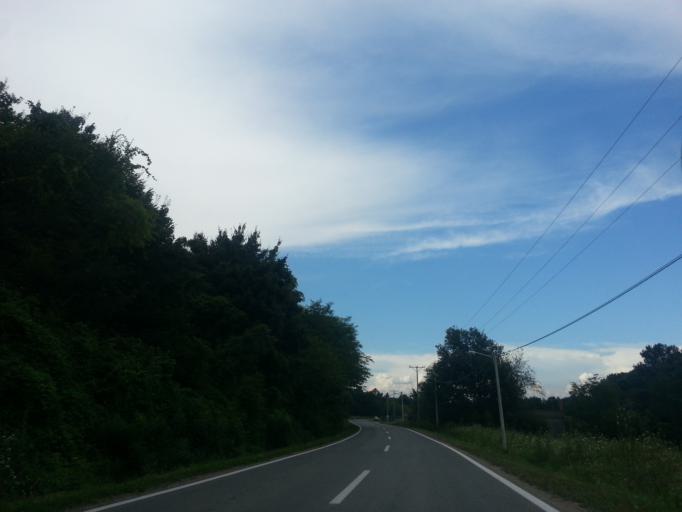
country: BA
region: Brcko
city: Brcko
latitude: 44.7898
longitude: 18.8167
